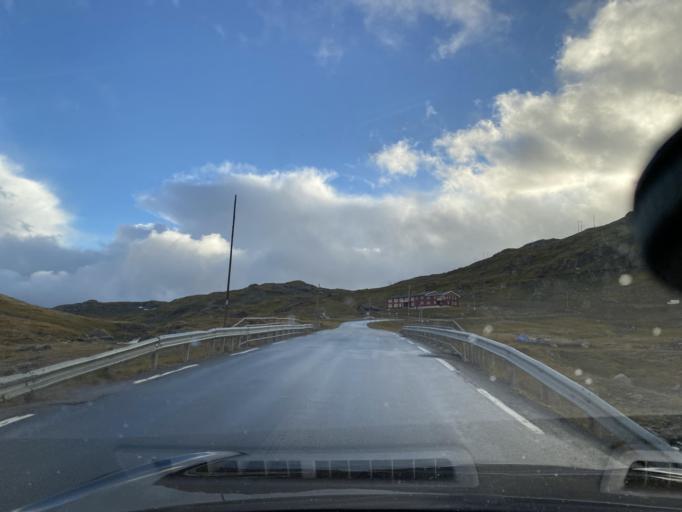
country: NO
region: Sogn og Fjordane
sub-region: Ardal
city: Farnes
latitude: 61.5760
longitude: 8.0358
